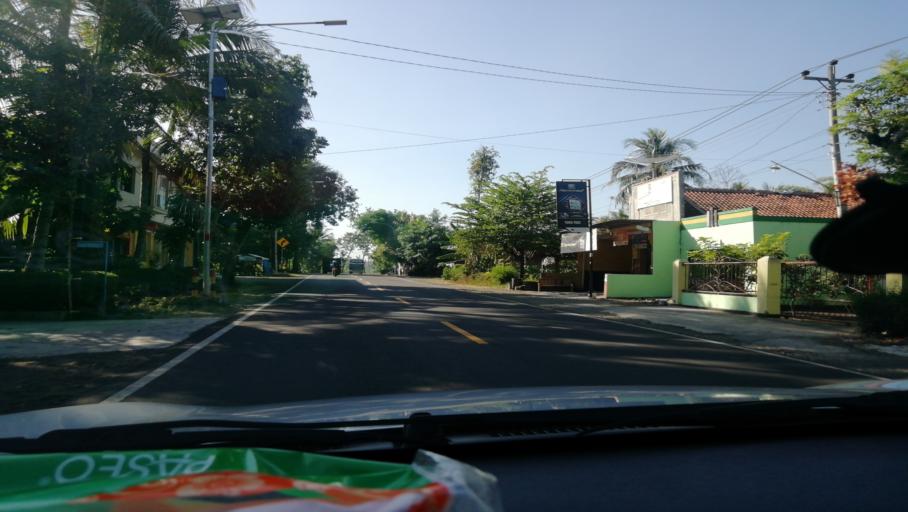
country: ID
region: Central Java
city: Kutoarjo
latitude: -7.7343
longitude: 109.9828
